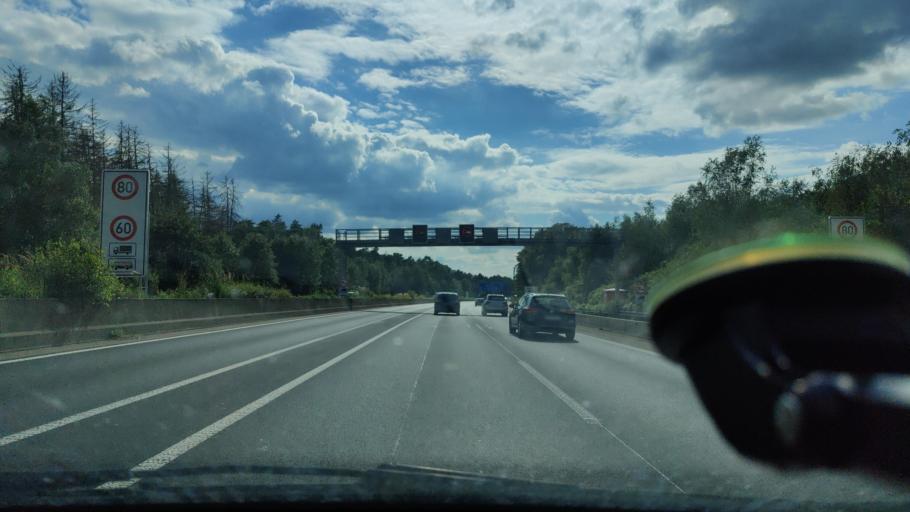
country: DE
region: North Rhine-Westphalia
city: Opladen
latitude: 51.0503
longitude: 7.0392
